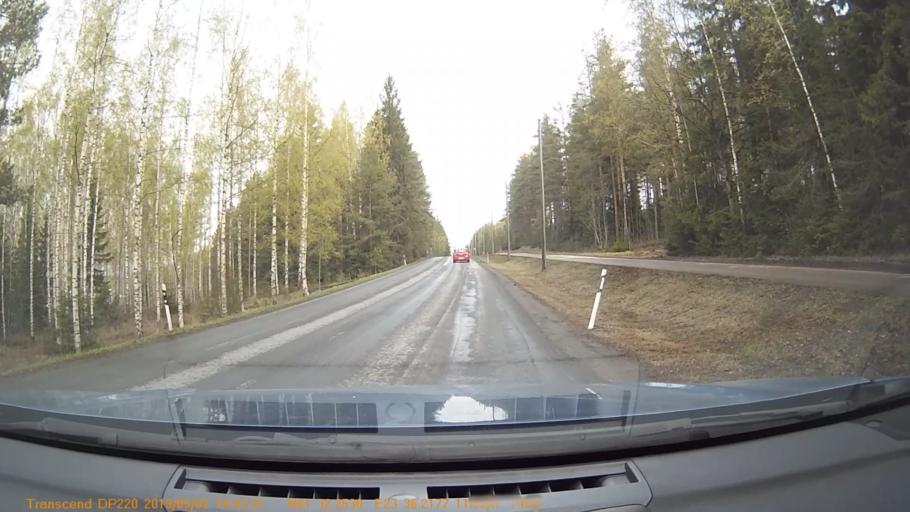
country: FI
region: Pirkanmaa
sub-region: Tampere
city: Yloejaervi
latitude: 61.5375
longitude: 23.6037
